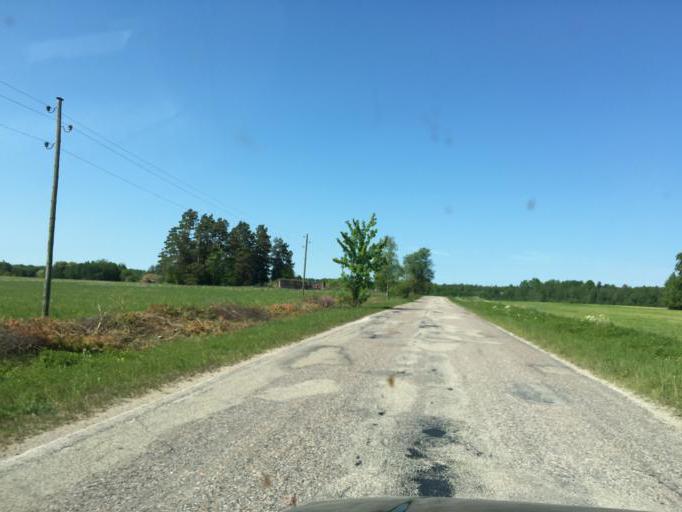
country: LV
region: Dundaga
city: Dundaga
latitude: 57.4628
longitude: 22.3223
